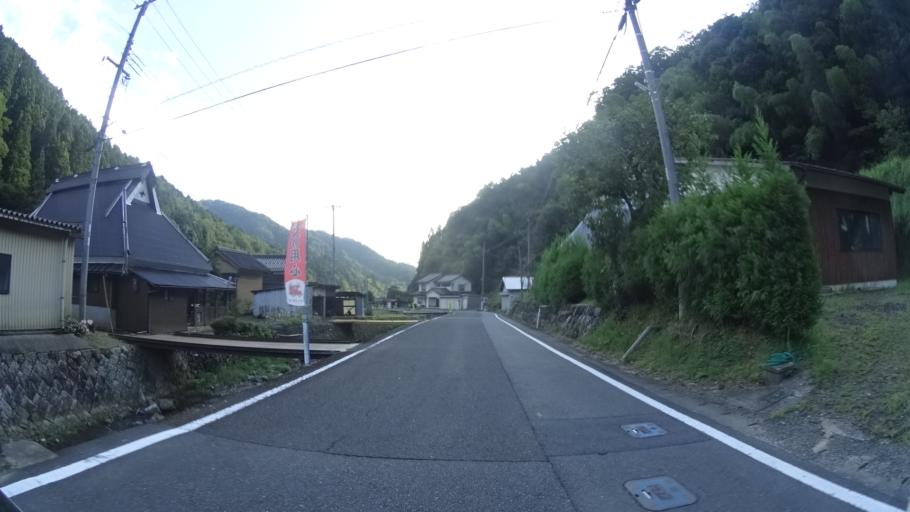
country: JP
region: Kyoto
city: Maizuru
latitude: 35.4269
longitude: 135.3865
